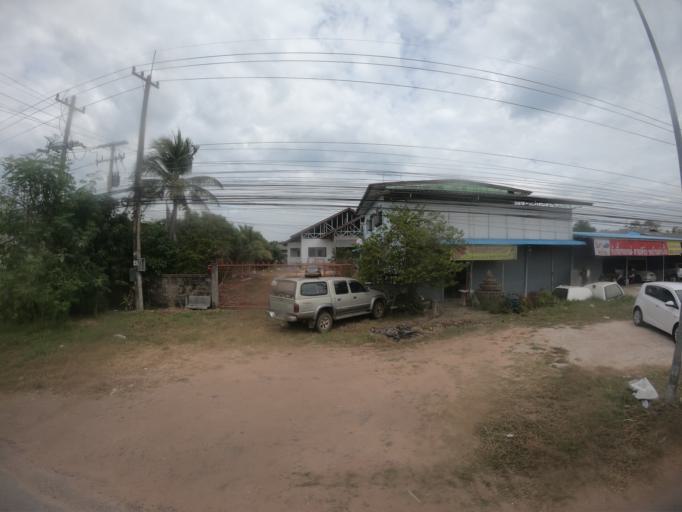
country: TH
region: Maha Sarakham
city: Maha Sarakham
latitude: 16.1658
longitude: 103.3322
